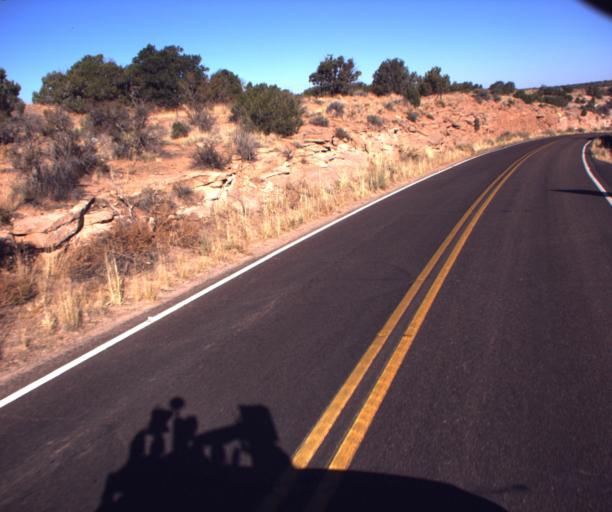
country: US
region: Arizona
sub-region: Navajo County
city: First Mesa
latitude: 35.8045
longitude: -110.1998
